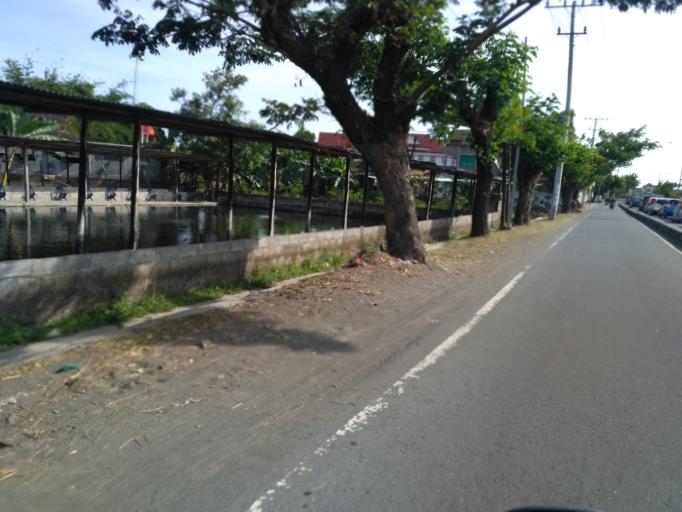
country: ID
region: Daerah Istimewa Yogyakarta
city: Sewon
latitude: -7.8363
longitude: 110.3792
